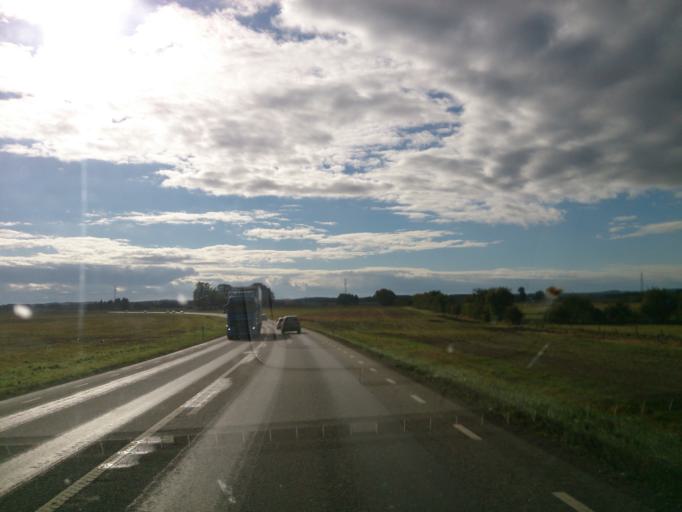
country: SE
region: Skane
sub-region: Sjobo Kommun
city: Sjoebo
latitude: 55.6308
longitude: 13.6816
